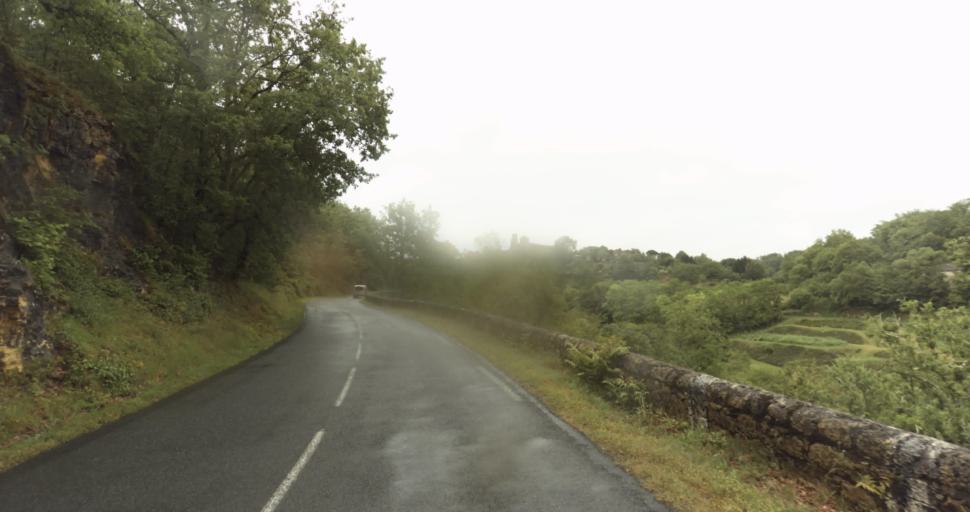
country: FR
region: Aquitaine
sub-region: Departement de la Dordogne
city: Beaumont-du-Perigord
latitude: 44.7721
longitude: 0.8113
